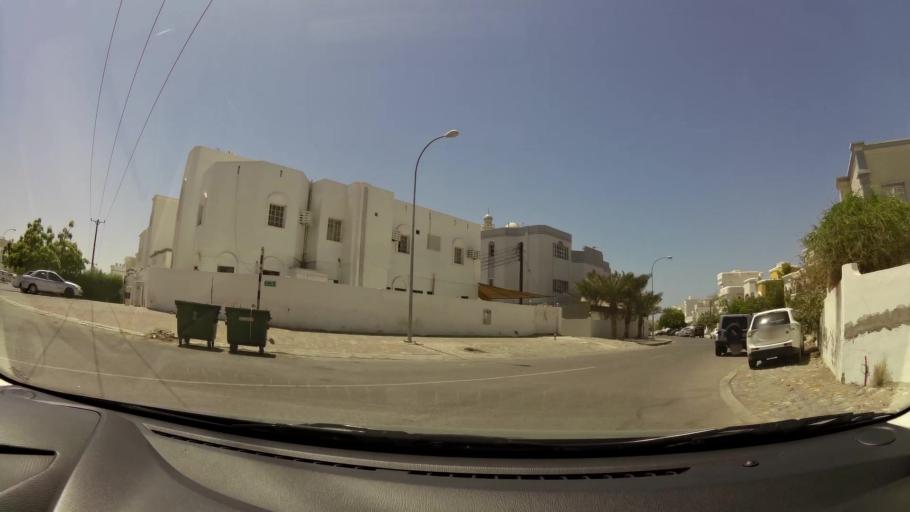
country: OM
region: Muhafazat Masqat
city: Bawshar
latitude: 23.5950
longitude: 58.3729
